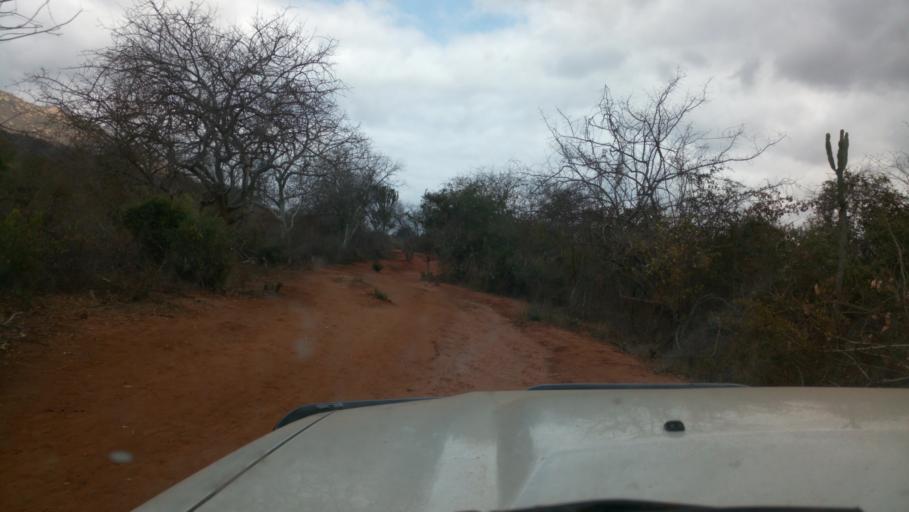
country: KE
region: Kitui
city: Kitui
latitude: -1.8543
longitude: 38.3571
